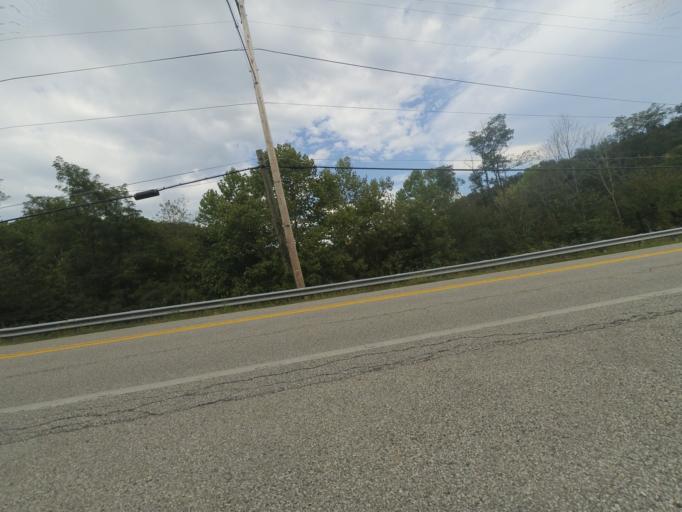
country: US
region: West Virginia
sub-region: Cabell County
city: Huntington
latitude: 38.3894
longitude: -82.4588
